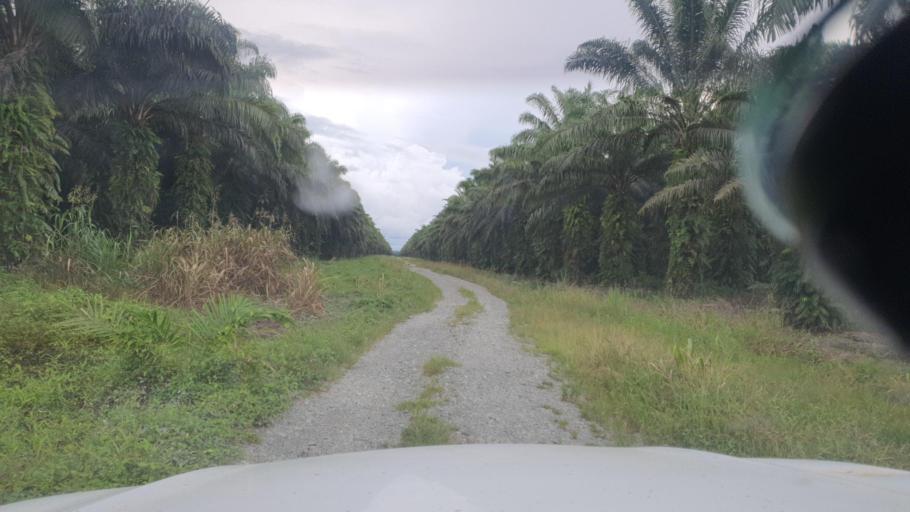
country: SB
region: Guadalcanal
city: Honiara
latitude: -9.4409
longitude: 160.2822
